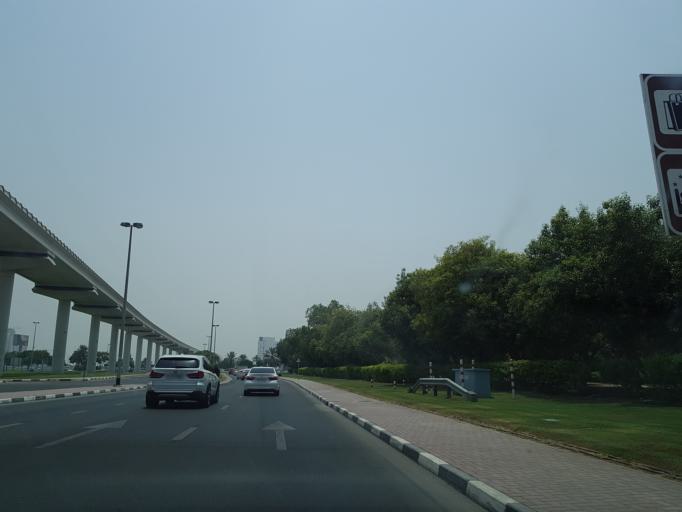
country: AE
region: Ash Shariqah
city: Sharjah
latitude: 25.2301
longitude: 55.3288
